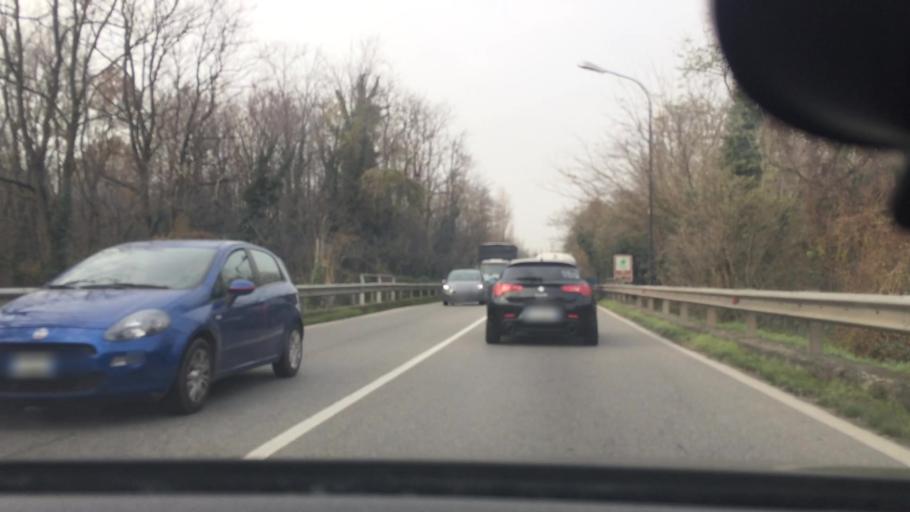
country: IT
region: Lombardy
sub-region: Provincia di Monza e Brianza
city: Villaggio del Sole
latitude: 45.6189
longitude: 9.1164
